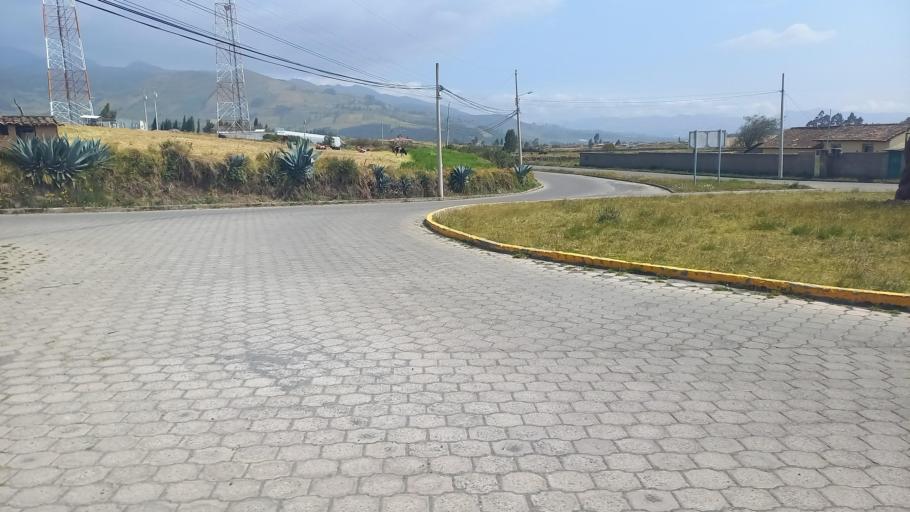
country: EC
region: Pichincha
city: Cayambe
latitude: 0.1497
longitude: -78.0706
